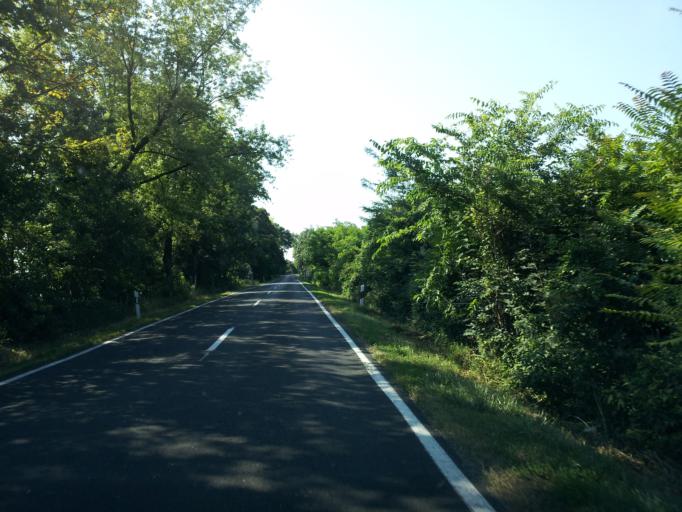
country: HU
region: Fejer
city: Bicske
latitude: 47.4066
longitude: 18.5843
